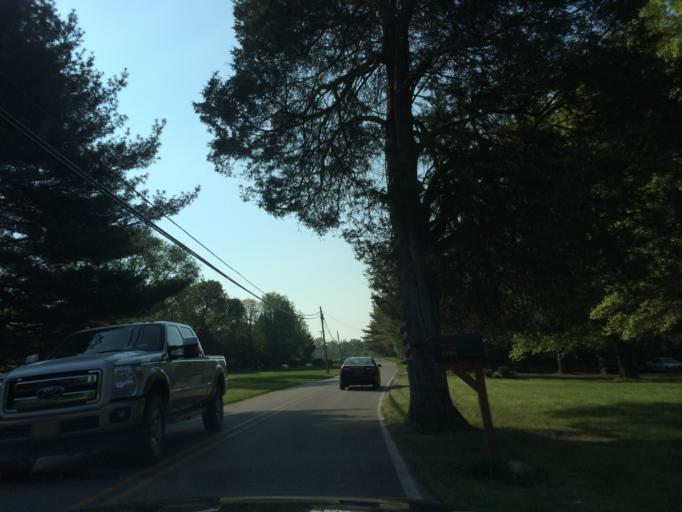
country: US
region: Maryland
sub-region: Howard County
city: Highland
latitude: 39.2192
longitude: -76.9991
